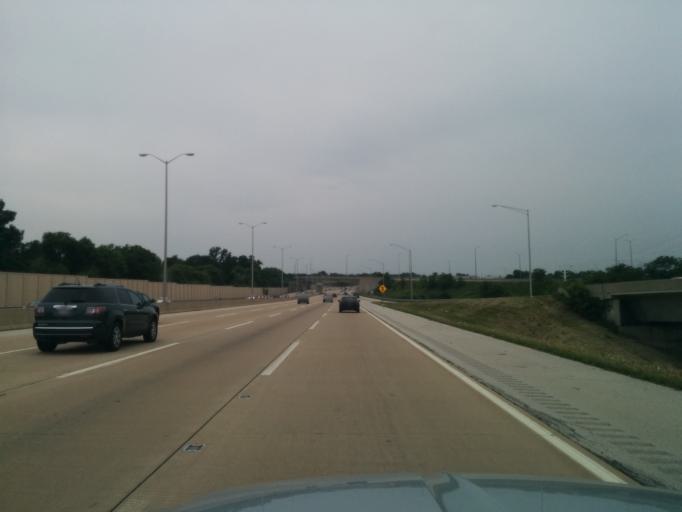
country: US
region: Illinois
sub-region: DuPage County
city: Downers Grove
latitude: 41.8190
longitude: -88.0260
